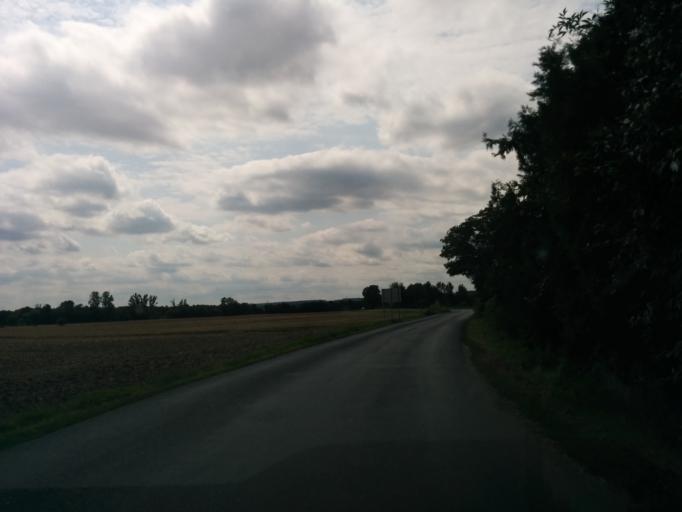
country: AT
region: Burgenland
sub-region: Politischer Bezirk Oberpullendorf
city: Lutzmannsburg
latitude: 47.4491
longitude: 16.6866
